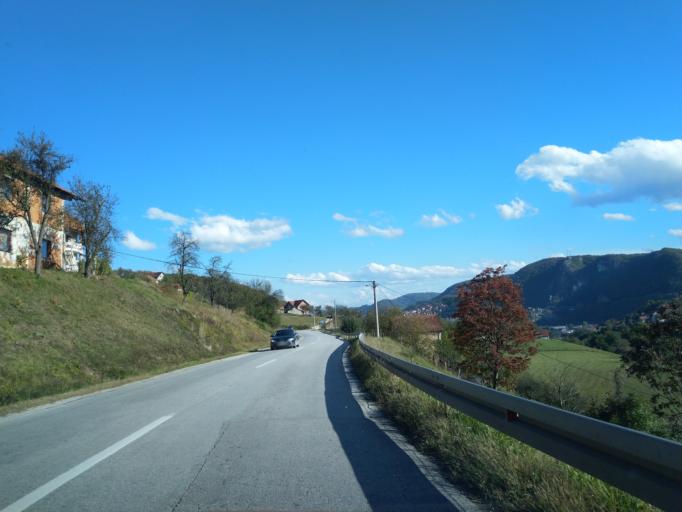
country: RS
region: Central Serbia
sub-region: Zlatiborski Okrug
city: Uzice
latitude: 43.8666
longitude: 19.8046
